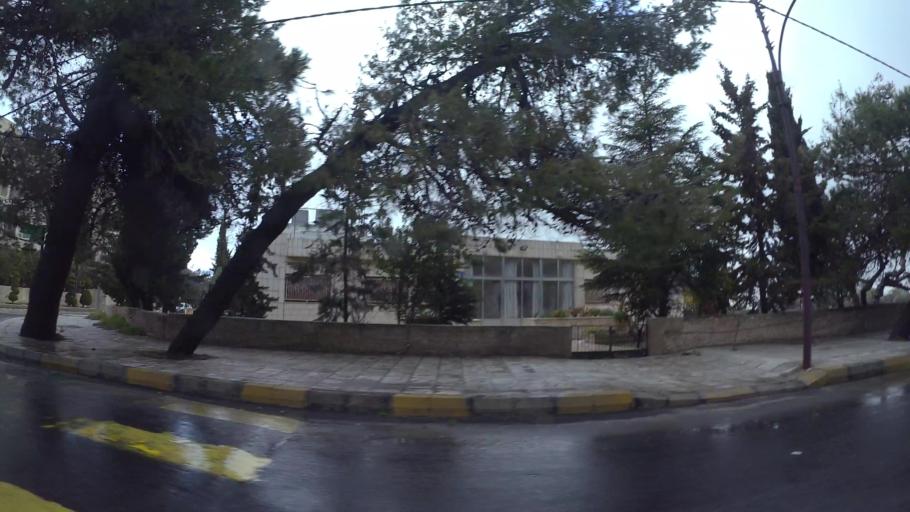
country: JO
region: Amman
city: Al Jubayhah
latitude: 32.0300
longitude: 35.8586
